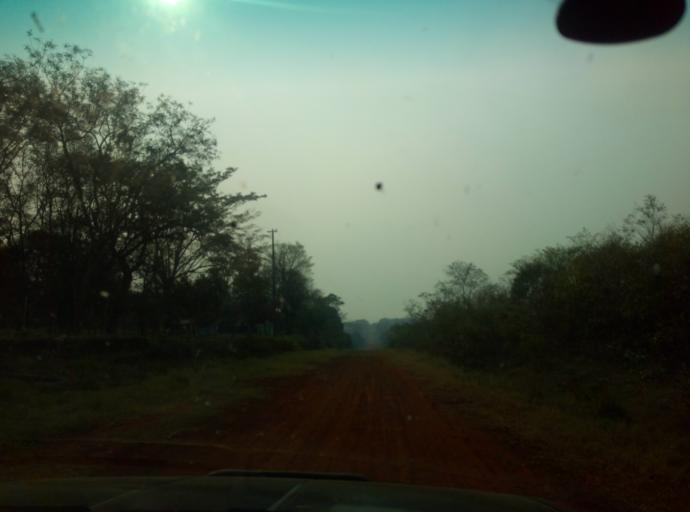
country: PY
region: Caaguazu
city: Carayao
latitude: -25.2039
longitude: -56.2379
